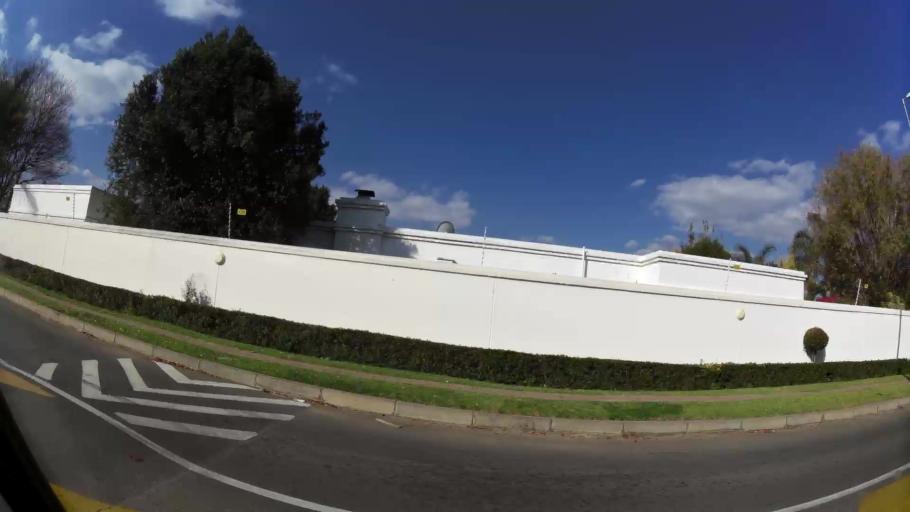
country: ZA
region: Gauteng
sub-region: City of Johannesburg Metropolitan Municipality
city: Diepsloot
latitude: -26.0200
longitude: 28.0165
